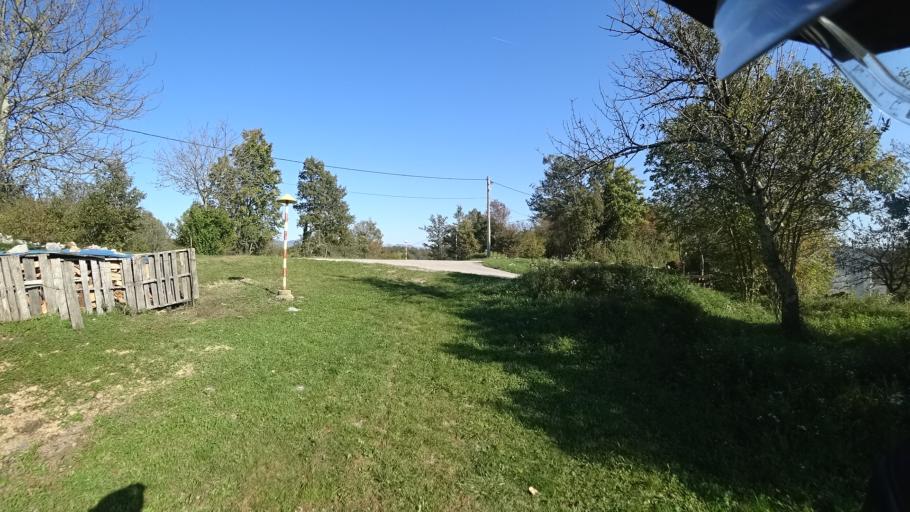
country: HR
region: Primorsko-Goranska
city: Matulji
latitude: 45.3883
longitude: 14.3164
